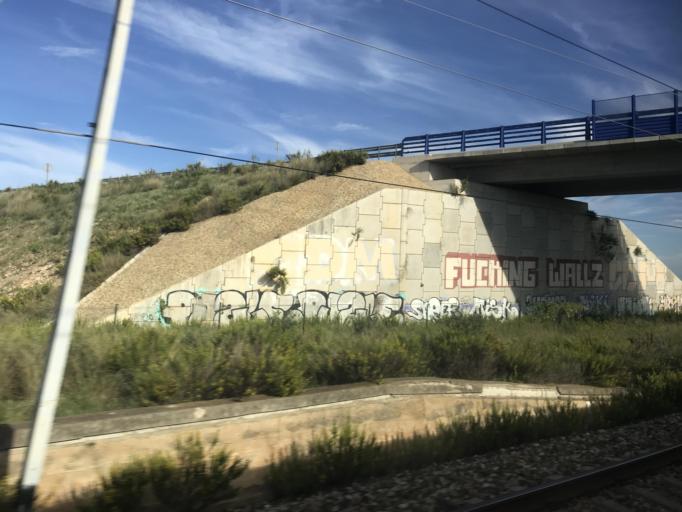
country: ES
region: Valencia
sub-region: Provincia de Castello
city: Vinaros
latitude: 40.4960
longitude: 0.4614
